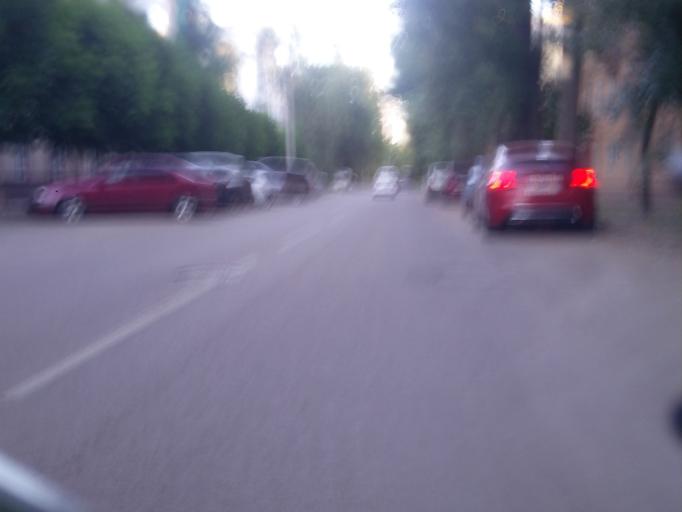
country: RU
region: Voronezj
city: Voronezh
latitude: 51.6504
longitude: 39.1706
